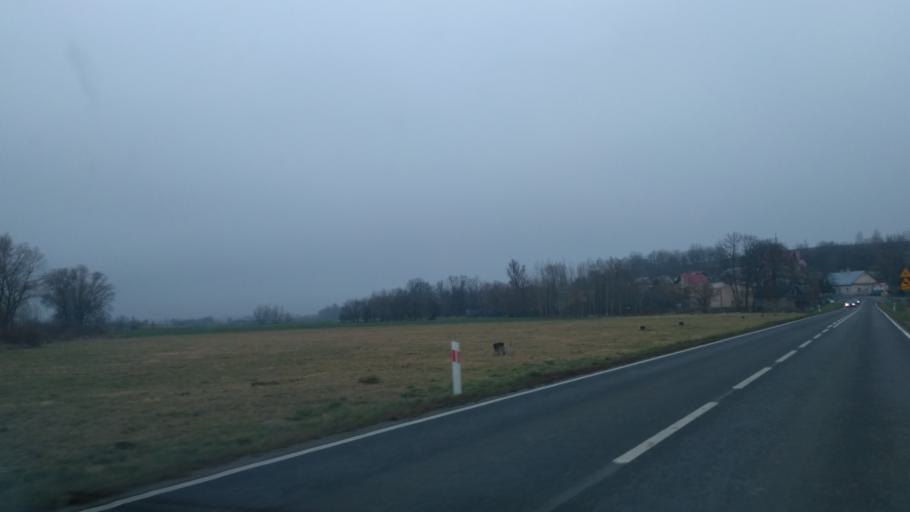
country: PL
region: Subcarpathian Voivodeship
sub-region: Powiat jaroslawski
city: Pruchnik
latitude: 49.9276
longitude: 22.5715
